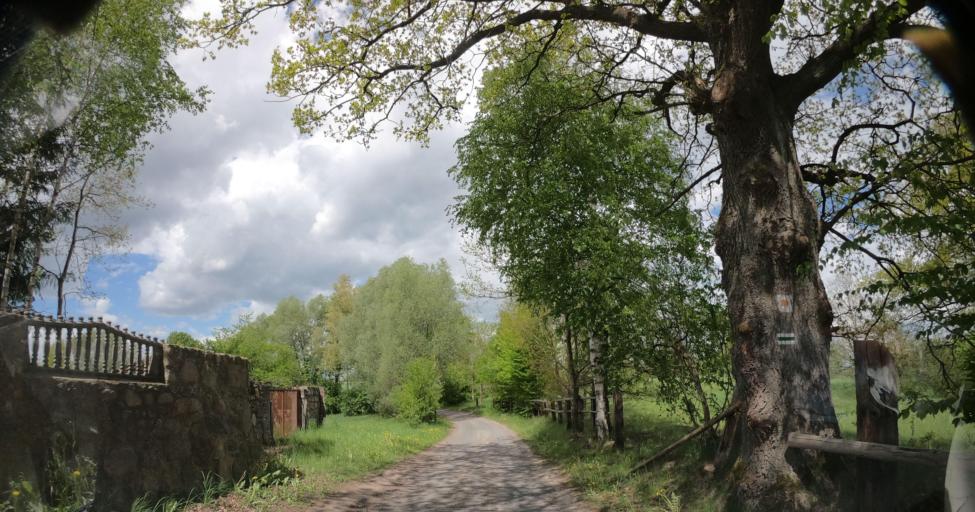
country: PL
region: West Pomeranian Voivodeship
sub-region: Powiat drawski
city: Drawsko Pomorskie
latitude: 53.5773
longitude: 15.7604
